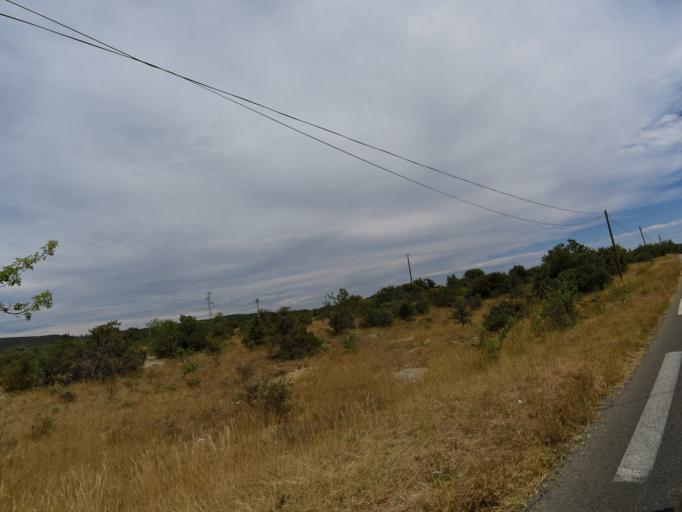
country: FR
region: Languedoc-Roussillon
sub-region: Departement du Gard
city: Sauve
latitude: 43.9434
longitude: 3.9242
